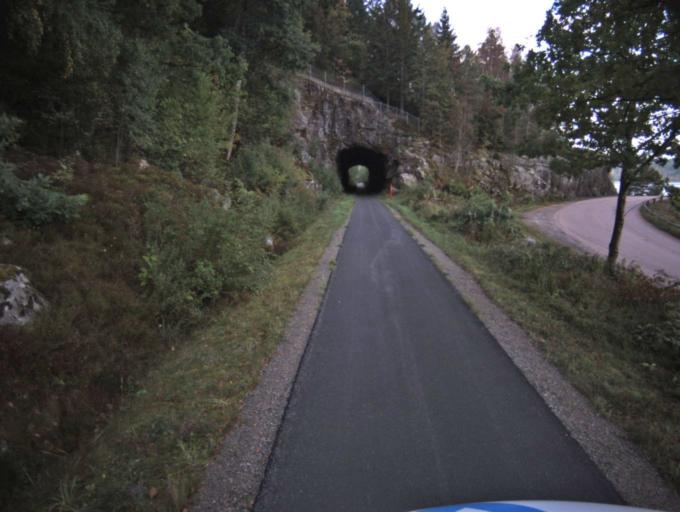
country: SE
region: Vaestra Goetaland
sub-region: Ulricehamns Kommun
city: Ulricehamn
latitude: 57.7552
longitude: 13.3976
